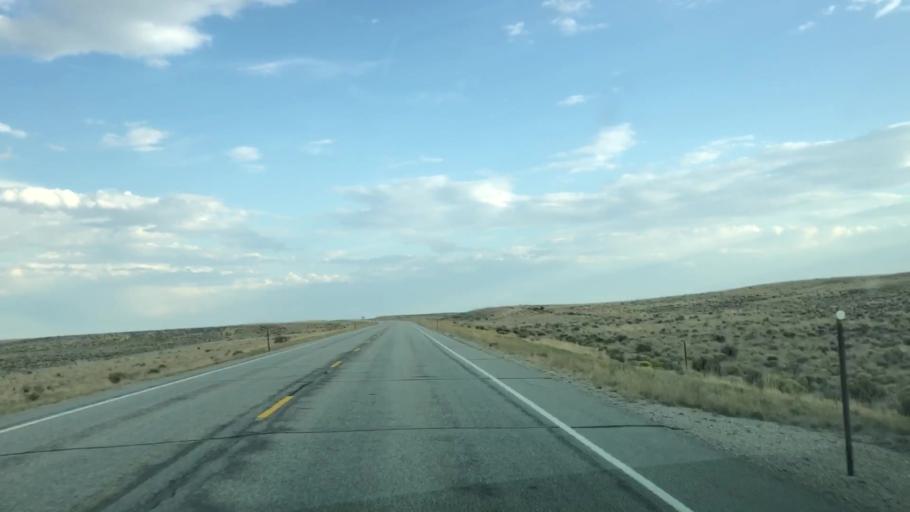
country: US
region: Wyoming
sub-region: Sweetwater County
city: North Rock Springs
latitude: 42.2837
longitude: -109.4872
